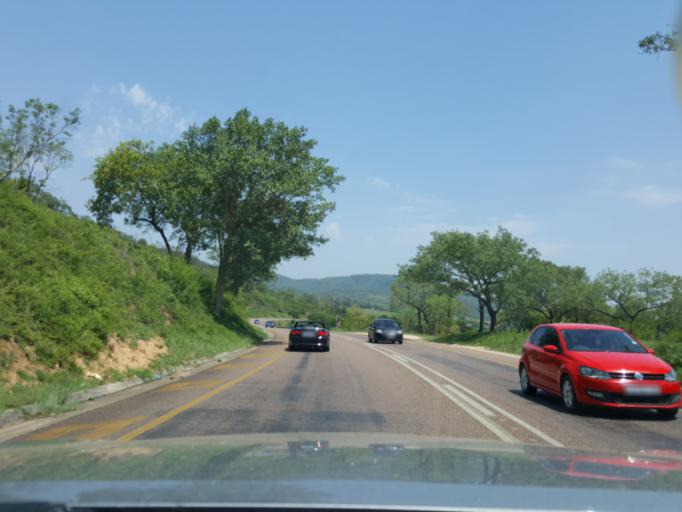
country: ZA
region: Mpumalanga
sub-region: Ehlanzeni District
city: Graksop
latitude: -25.0225
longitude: 31.1225
